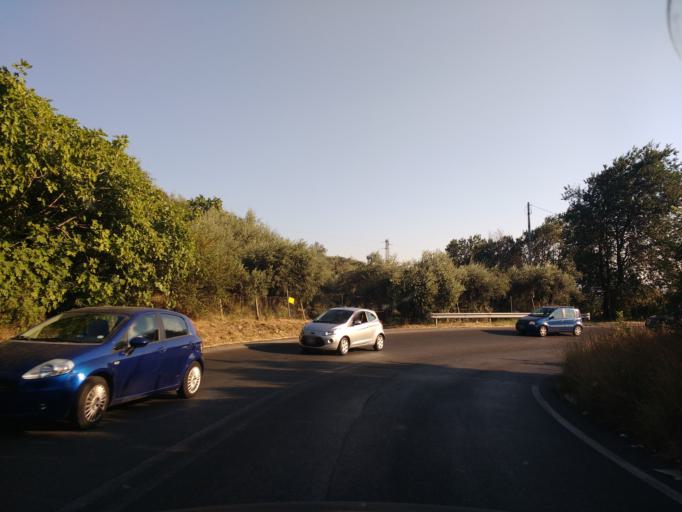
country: IT
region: Latium
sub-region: Citta metropolitana di Roma Capitale
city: Tivoli
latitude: 41.9480
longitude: 12.7931
